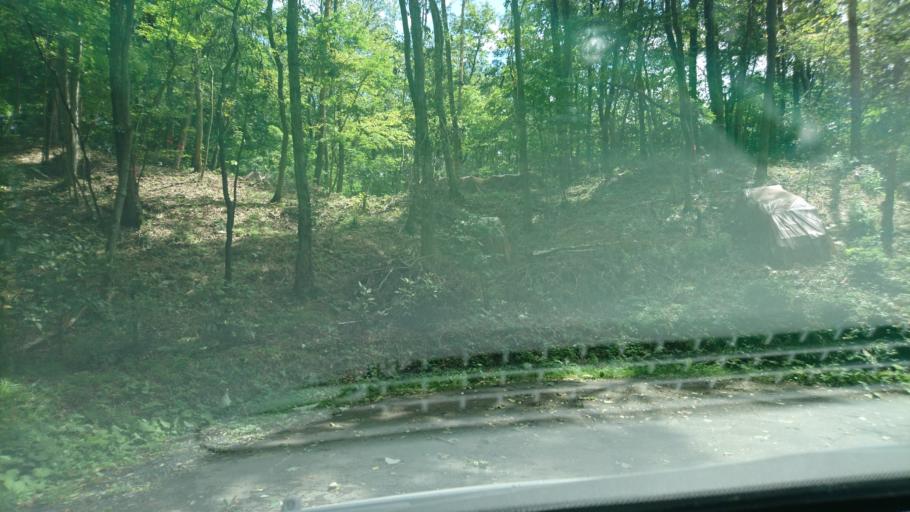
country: JP
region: Iwate
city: Ichinoseki
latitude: 38.9429
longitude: 141.1218
